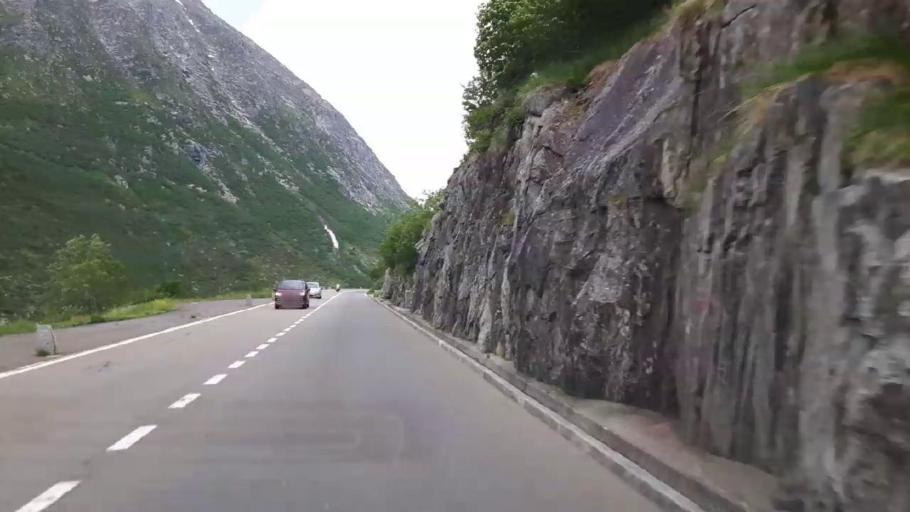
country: CH
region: Uri
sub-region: Uri
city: Andermatt
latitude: 46.5988
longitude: 8.5630
